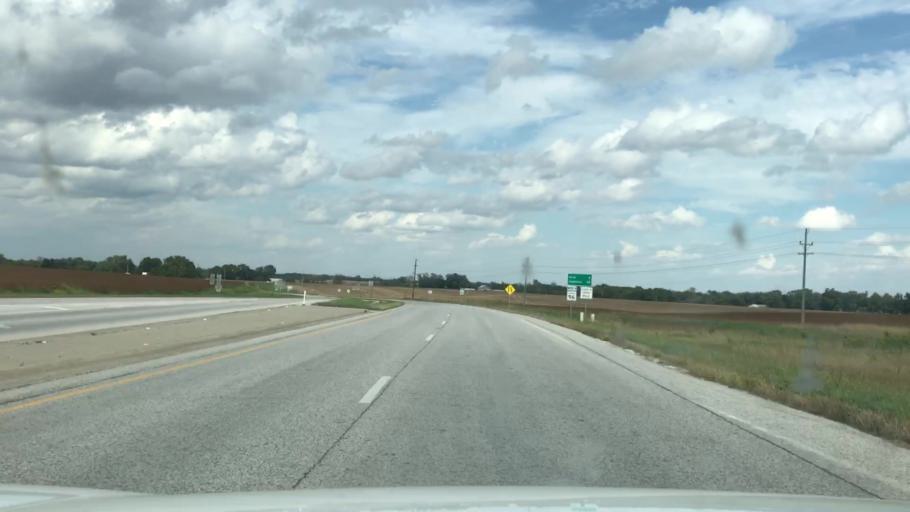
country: US
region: Illinois
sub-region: Adams County
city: Quincy
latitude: 40.0087
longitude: -91.3678
